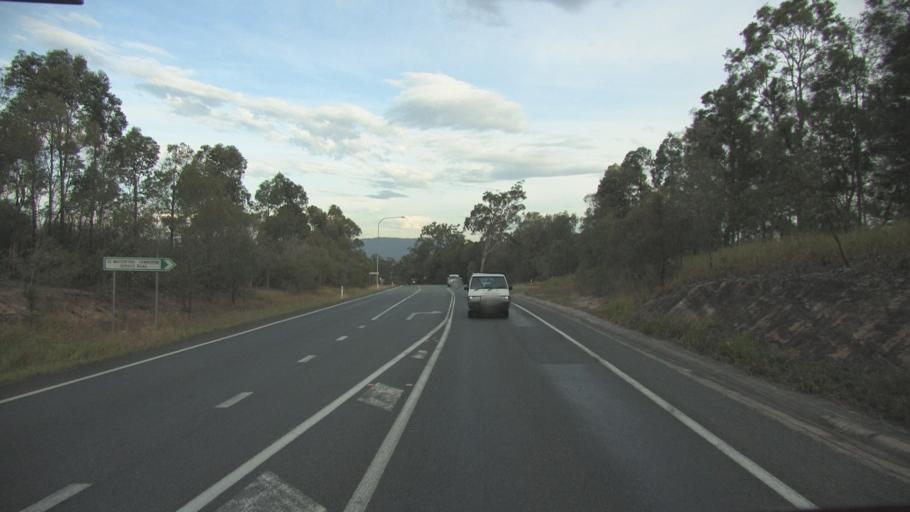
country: AU
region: Queensland
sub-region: Logan
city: Chambers Flat
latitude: -27.8353
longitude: 153.1077
